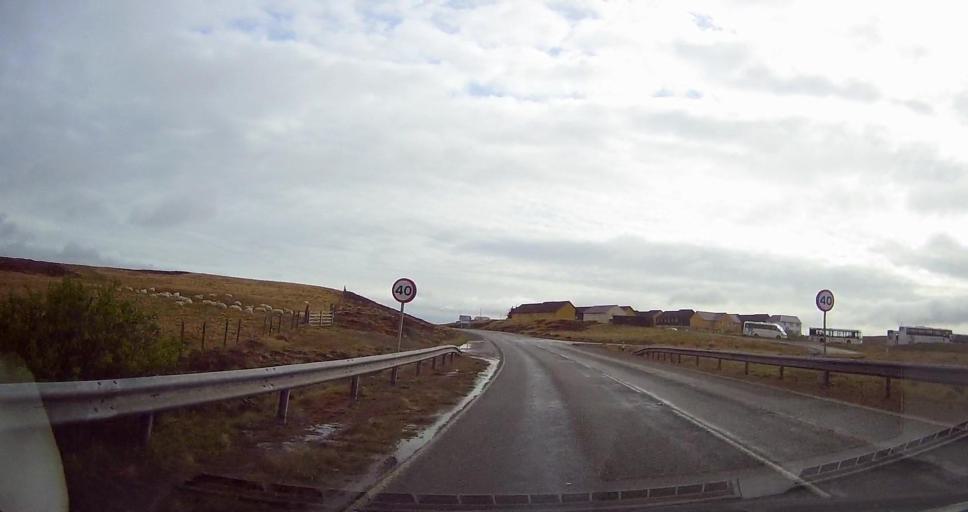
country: GB
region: Scotland
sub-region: Shetland Islands
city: Lerwick
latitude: 60.1385
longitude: -1.1909
